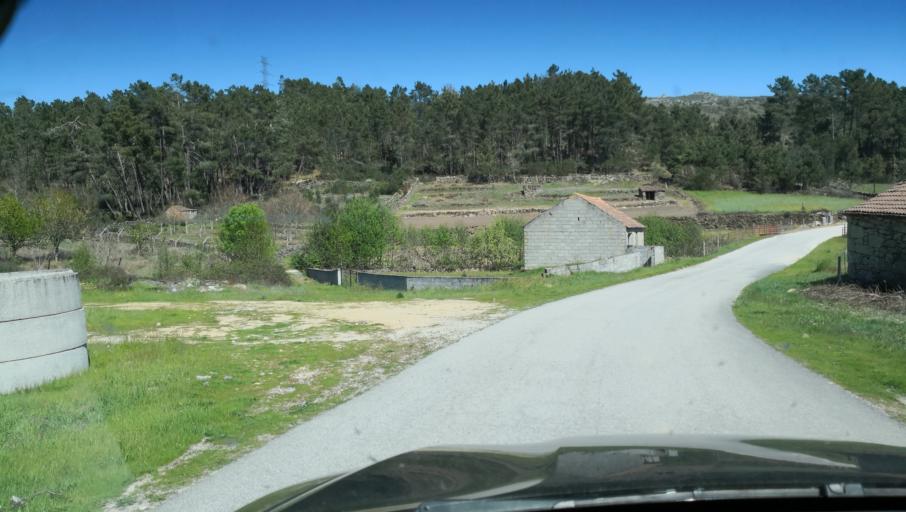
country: PT
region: Vila Real
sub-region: Sabrosa
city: Sabrosa
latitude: 41.3001
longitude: -7.6414
